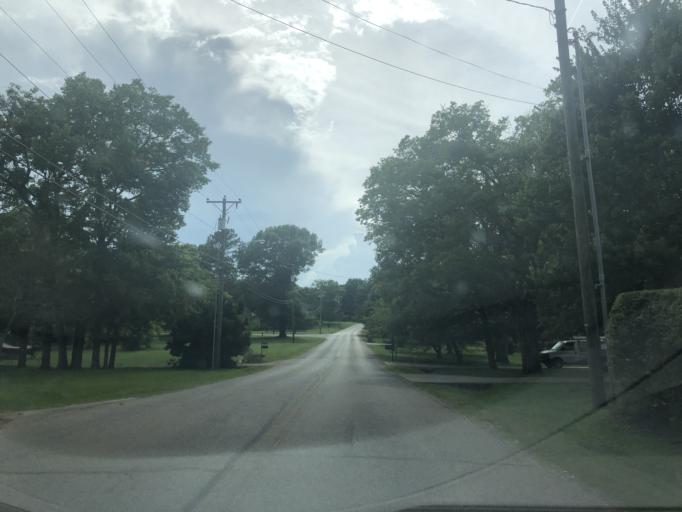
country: US
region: Tennessee
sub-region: Davidson County
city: Oak Hill
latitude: 36.0826
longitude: -86.7781
